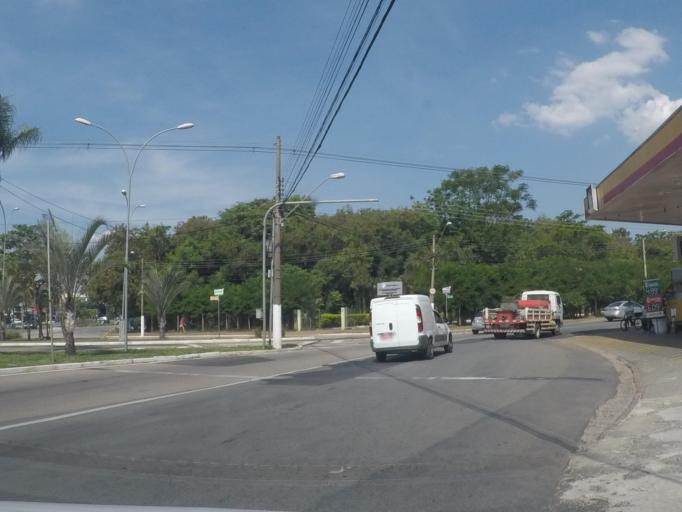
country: BR
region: Sao Paulo
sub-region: Sumare
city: Sumare
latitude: -22.8184
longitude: -47.2653
